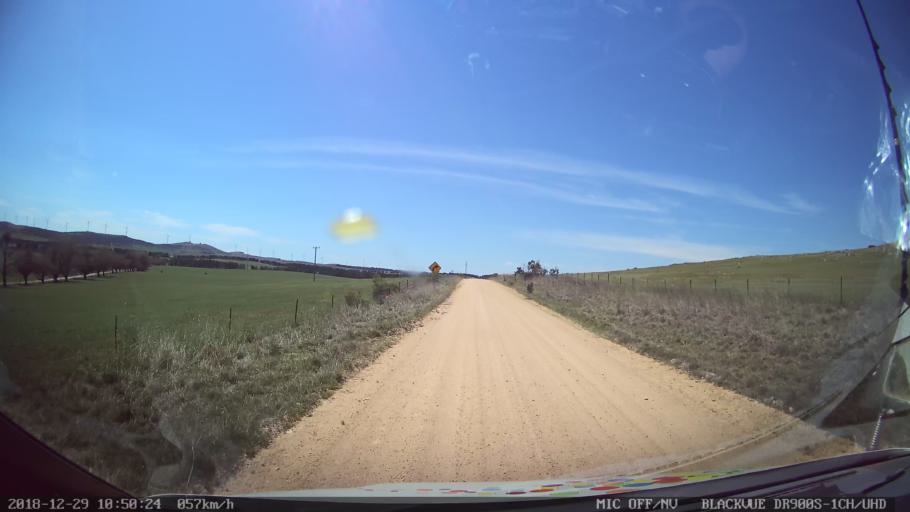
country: AU
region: New South Wales
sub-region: Palerang
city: Bungendore
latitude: -35.0815
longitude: 149.5223
